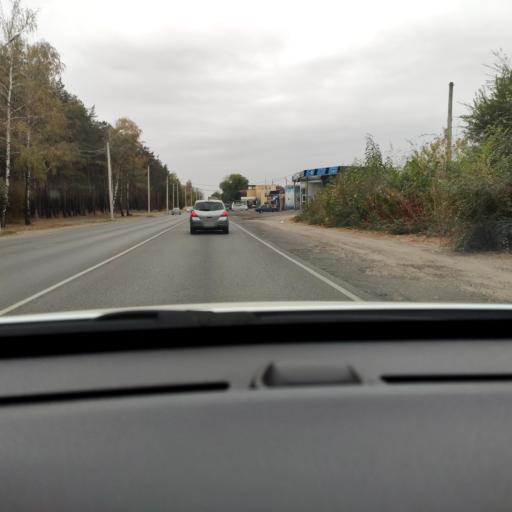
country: RU
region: Voronezj
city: Voronezh
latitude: 51.6740
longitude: 39.2726
